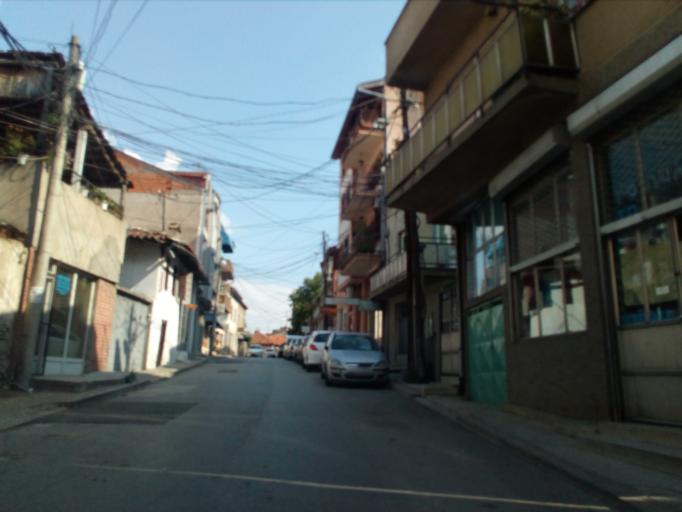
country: MK
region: Veles
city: Veles
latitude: 41.7165
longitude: 21.7822
